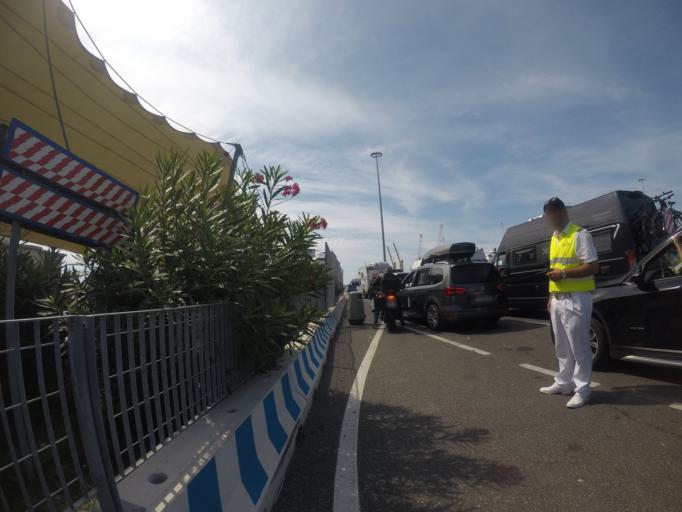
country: IT
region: Tuscany
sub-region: Provincia di Livorno
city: Livorno
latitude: 43.5537
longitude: 10.3016
